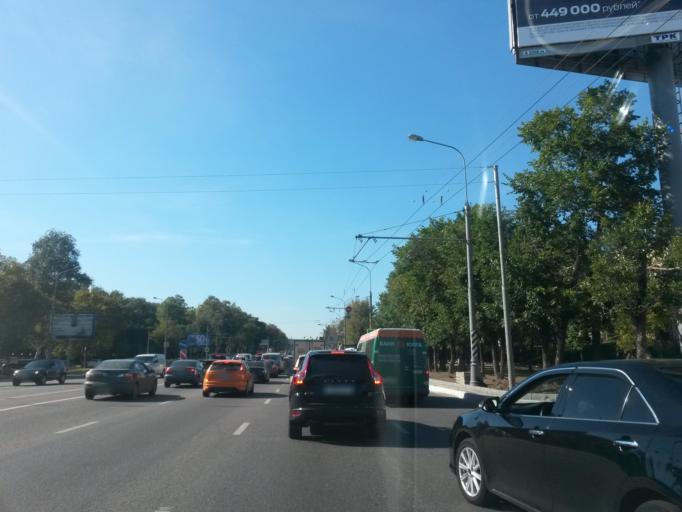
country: RU
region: Moscow
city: Tsaritsyno
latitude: 55.6560
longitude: 37.6472
